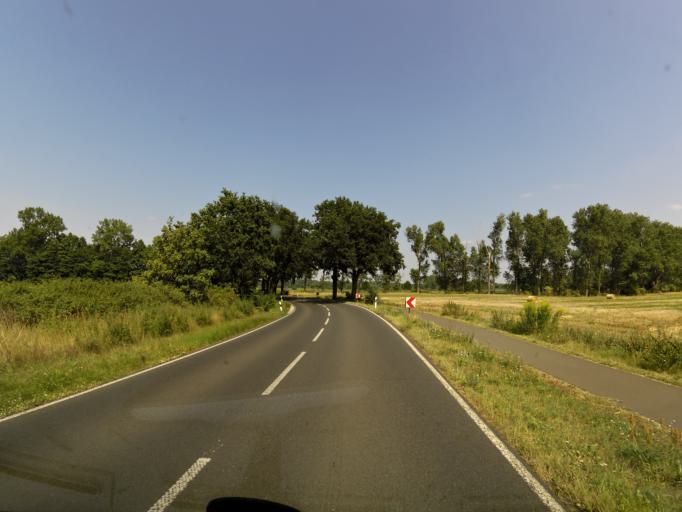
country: DE
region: Brandenburg
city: Liebenwalde
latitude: 52.8539
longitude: 13.3313
